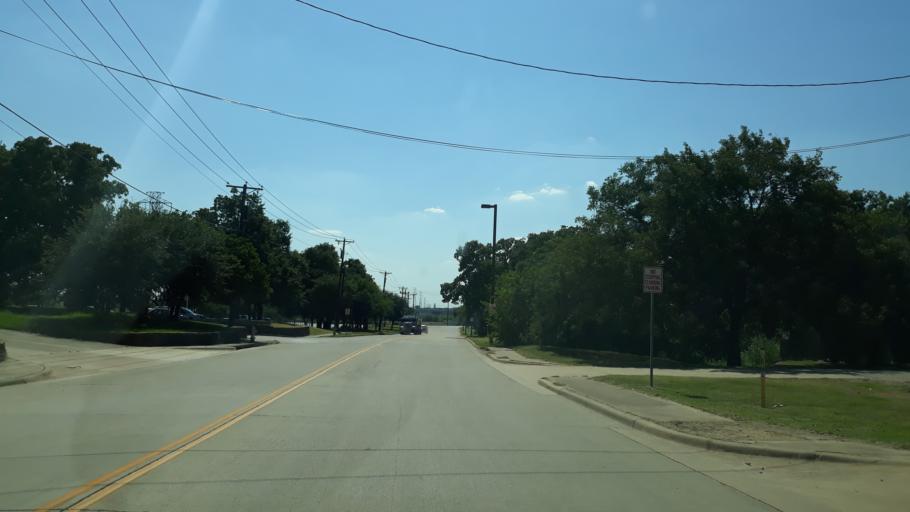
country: US
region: Texas
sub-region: Dallas County
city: Irving
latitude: 32.8173
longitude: -97.0052
